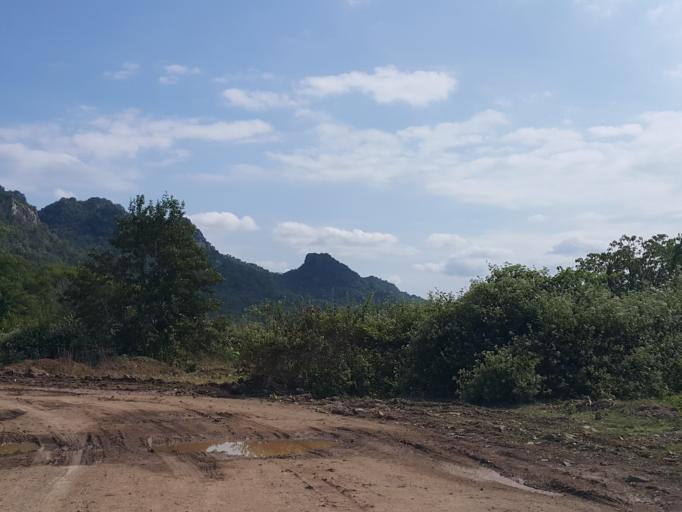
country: TH
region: Lampang
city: Mae Mo
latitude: 18.3306
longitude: 99.7569
